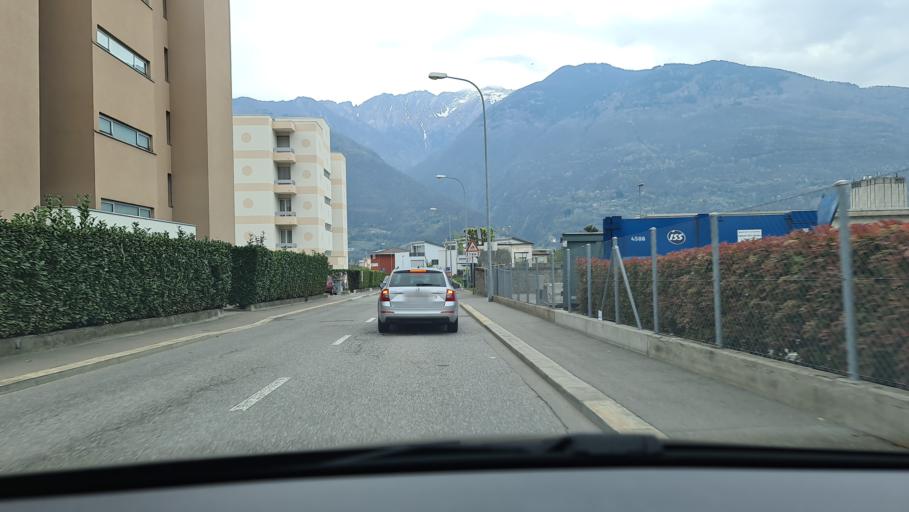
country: CH
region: Ticino
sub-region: Bellinzona District
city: Giubiasco
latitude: 46.1708
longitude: 9.0068
